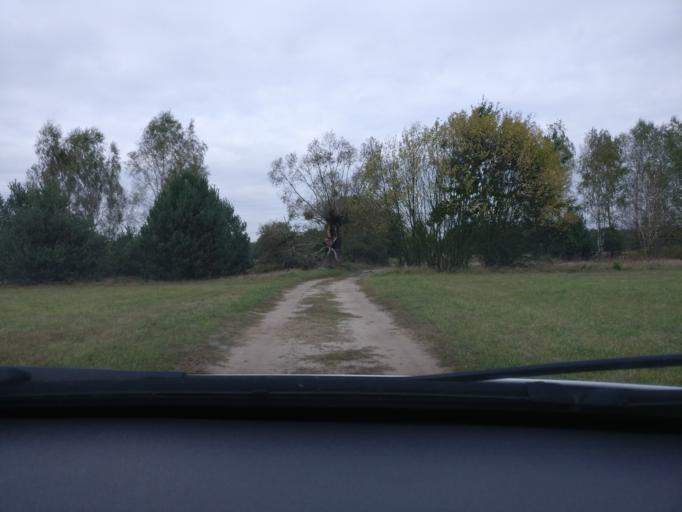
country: PL
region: Masovian Voivodeship
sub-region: Powiat kozienicki
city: Garbatka-Letnisko
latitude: 51.5182
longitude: 21.5994
